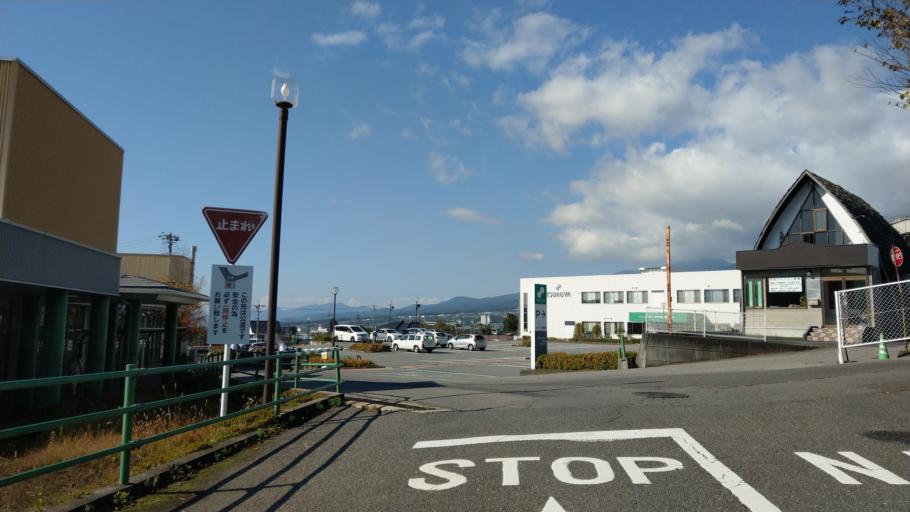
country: JP
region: Nagano
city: Komoro
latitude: 36.3170
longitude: 138.4367
